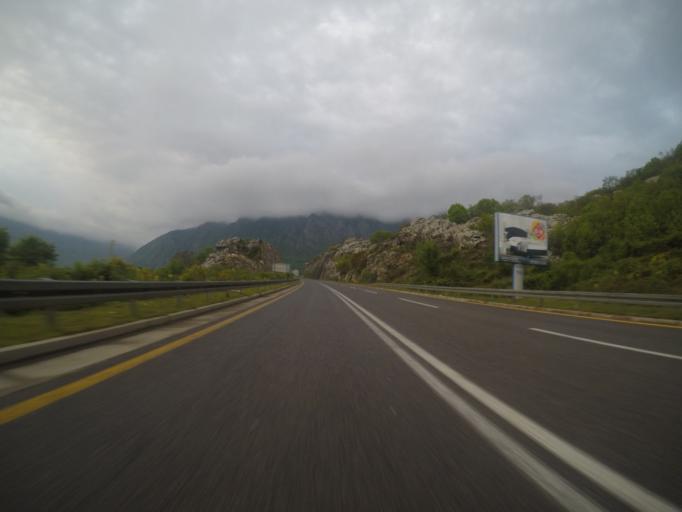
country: ME
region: Bar
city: Sutomore
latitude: 42.2101
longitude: 19.0483
